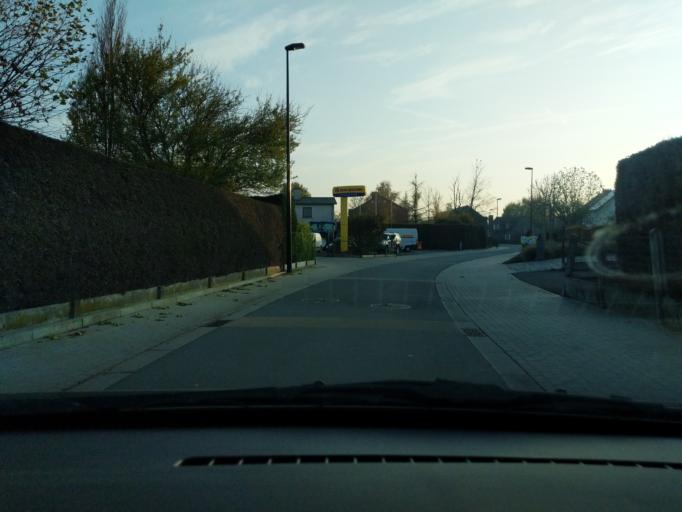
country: BE
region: Flanders
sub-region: Provincie Oost-Vlaanderen
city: Nevele
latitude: 51.0377
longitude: 3.5160
